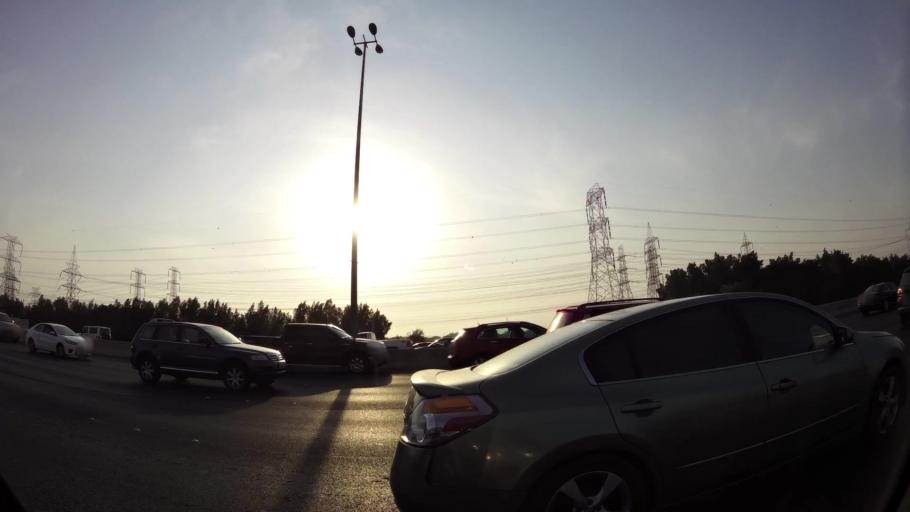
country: KW
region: Mubarak al Kabir
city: Sabah as Salim
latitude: 29.2241
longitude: 48.0547
